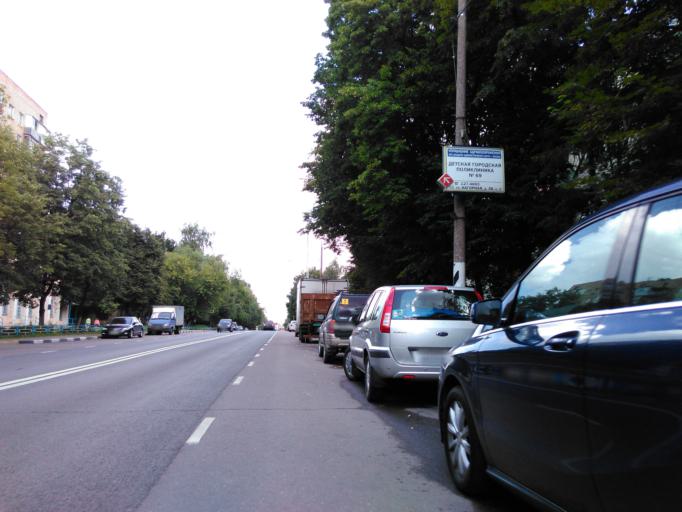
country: RU
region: Moscow
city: Kotlovka
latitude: 55.6710
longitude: 37.5933
